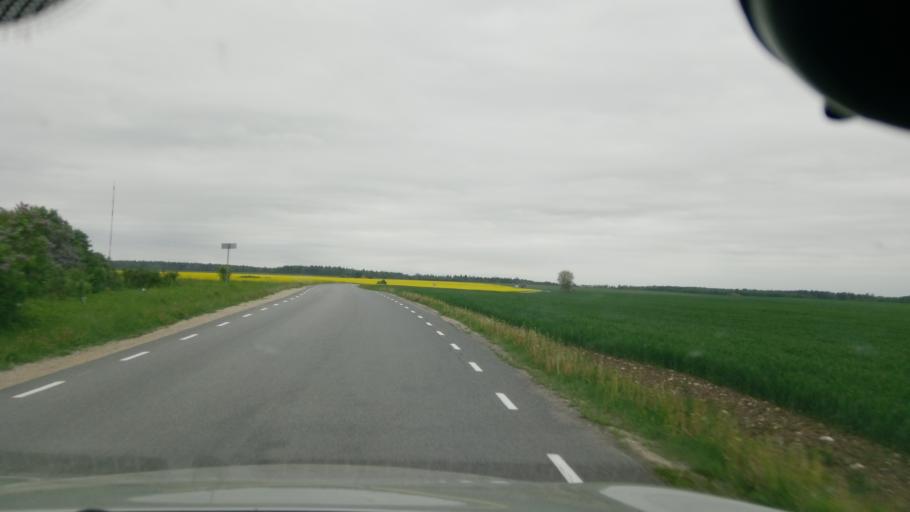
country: EE
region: Jaervamaa
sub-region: Koeru vald
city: Koeru
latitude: 59.0013
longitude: 26.0758
